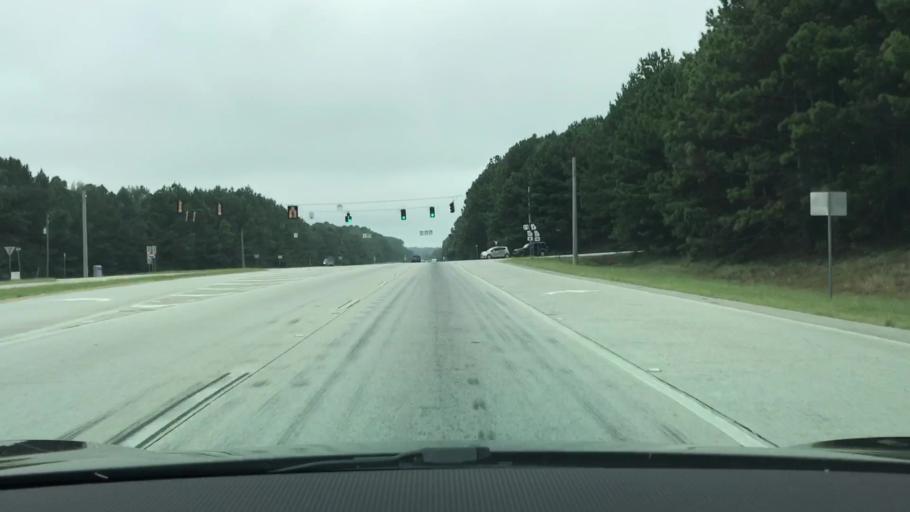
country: US
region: Georgia
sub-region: Barrow County
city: Statham
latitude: 33.9562
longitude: -83.6059
